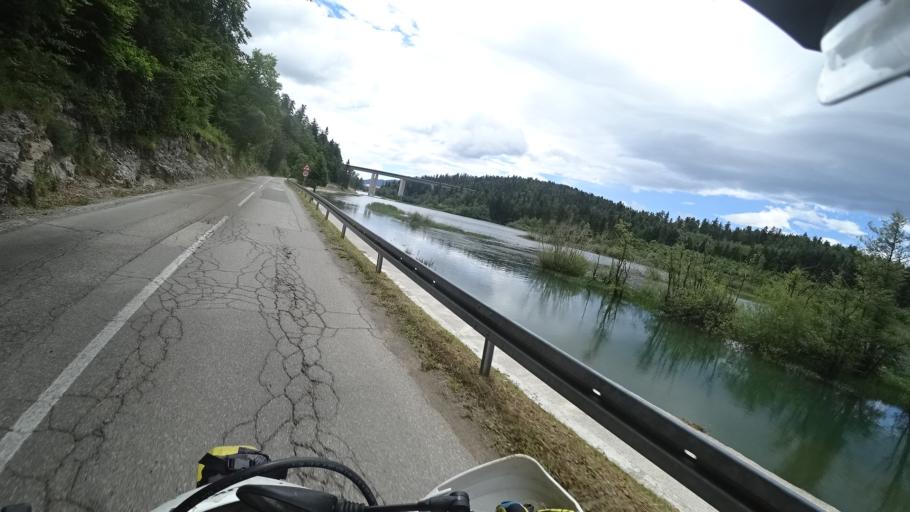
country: HR
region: Primorsko-Goranska
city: Hreljin
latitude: 45.3221
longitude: 14.7071
